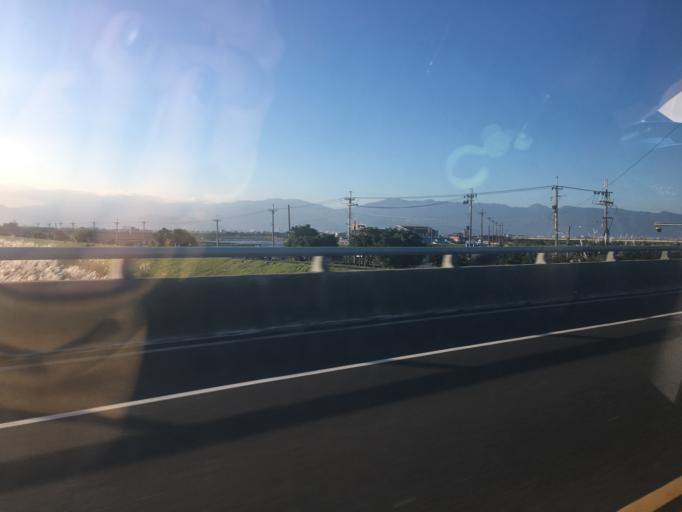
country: TW
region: Taiwan
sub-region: Yilan
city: Yilan
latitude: 24.7166
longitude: 121.8205
